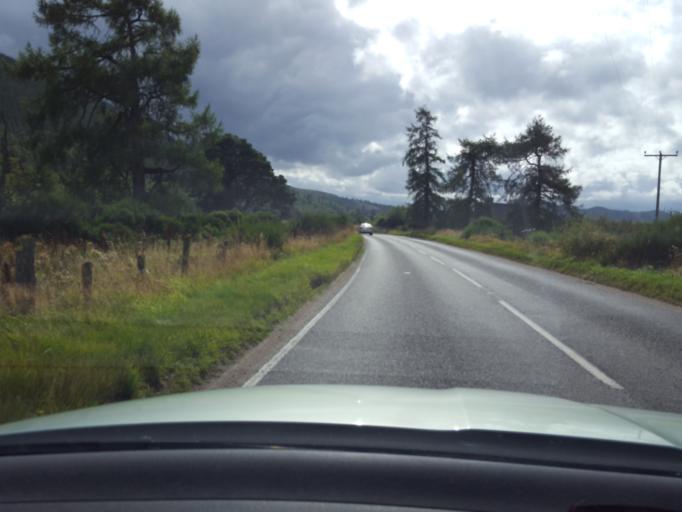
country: GB
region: Scotland
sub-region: Aberdeenshire
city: Ballater
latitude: 57.0552
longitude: -3.0278
